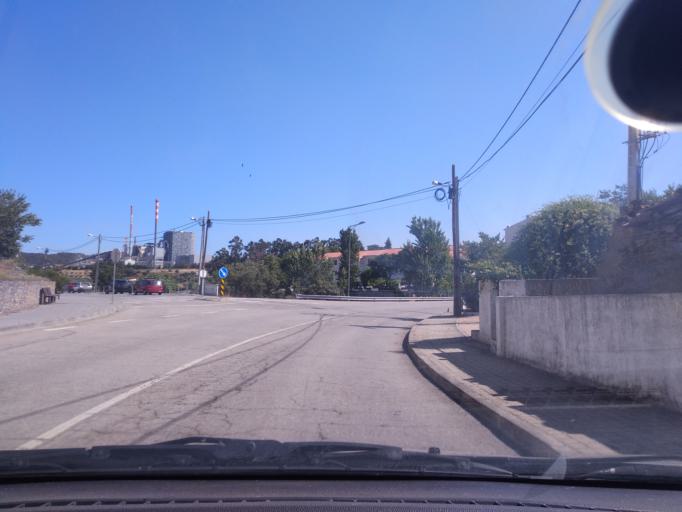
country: PT
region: Portalegre
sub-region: Nisa
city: Nisa
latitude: 39.6537
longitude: -7.6696
